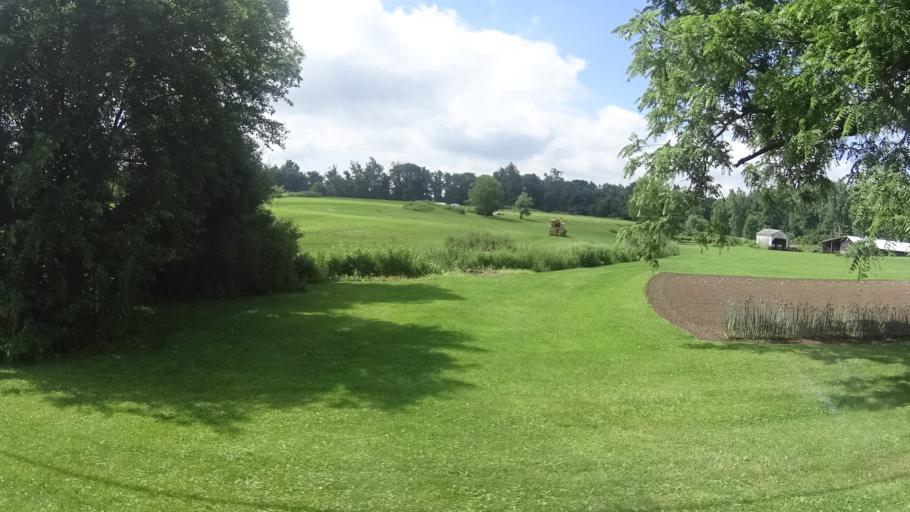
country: US
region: Ohio
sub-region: Huron County
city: Wakeman
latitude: 41.3130
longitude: -82.4121
